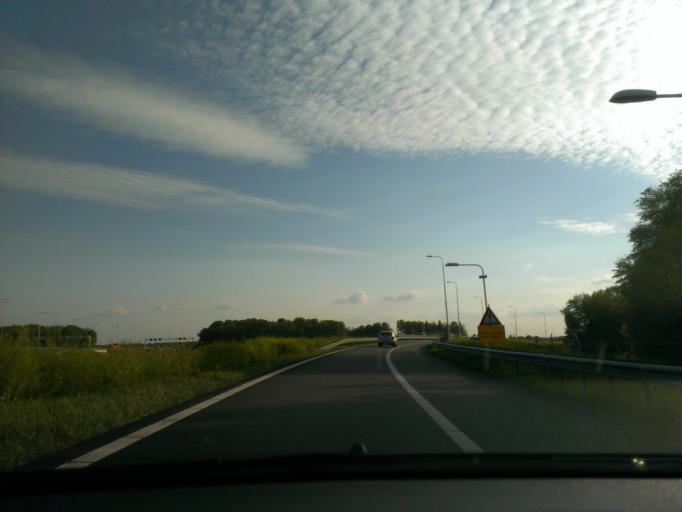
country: NL
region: Gelderland
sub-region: Gemeente Overbetuwe
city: Herveld
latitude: 51.9118
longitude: 5.7698
